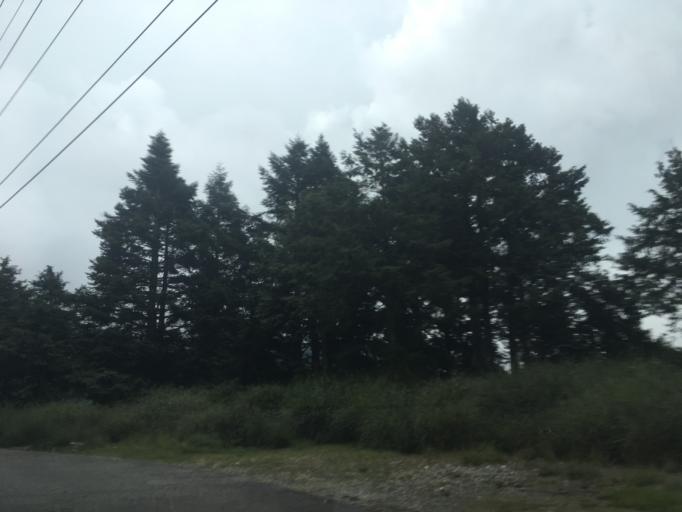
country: TW
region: Taiwan
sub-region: Nantou
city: Puli
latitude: 24.2718
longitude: 121.0337
